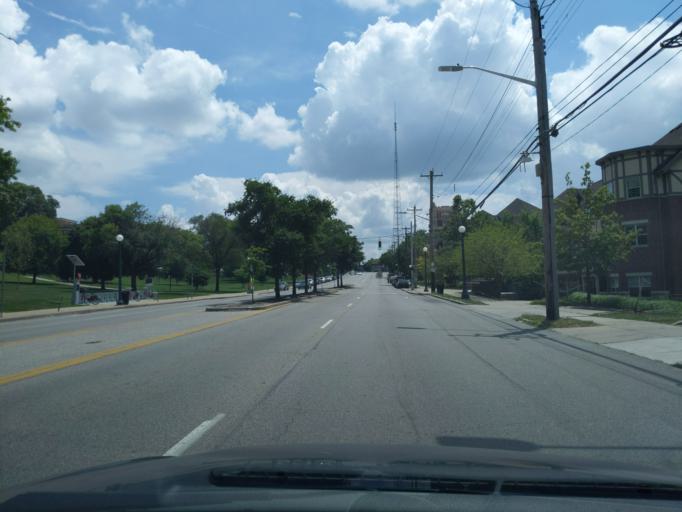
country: US
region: Ohio
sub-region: Hamilton County
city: Saint Bernard
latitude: 39.1319
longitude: -84.5205
